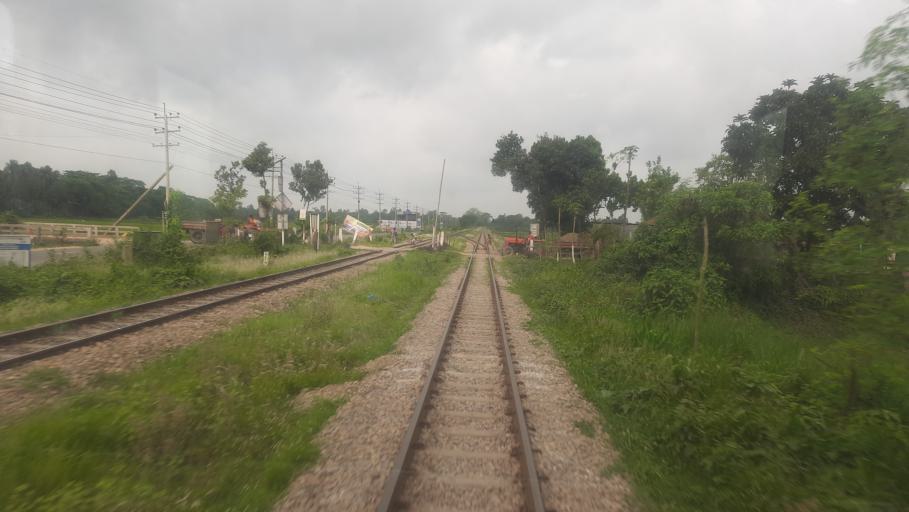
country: BD
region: Dhaka
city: Narsingdi
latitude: 23.9346
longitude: 90.7676
